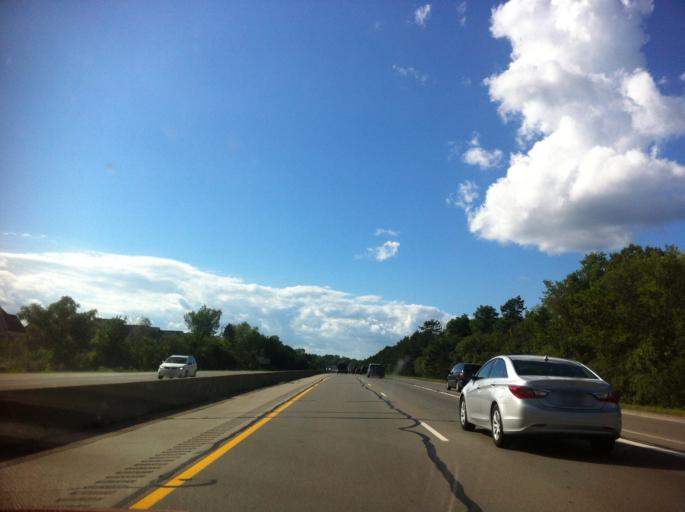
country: US
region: Michigan
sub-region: Washtenaw County
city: Ann Arbor
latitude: 42.2385
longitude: -83.7535
